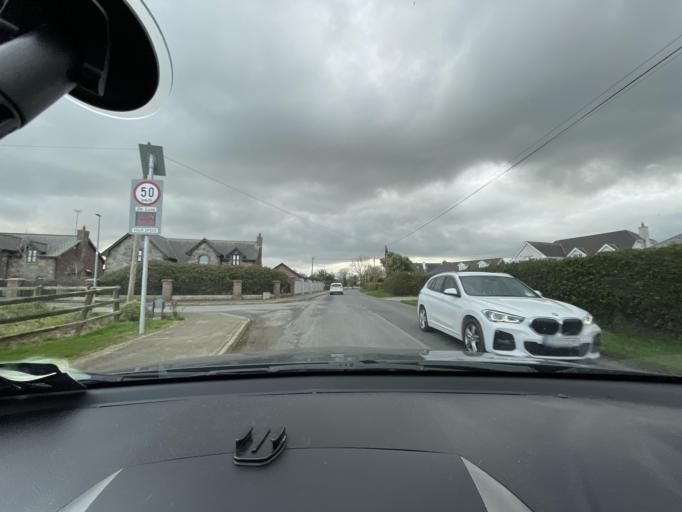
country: IE
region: Leinster
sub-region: Lu
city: Termonfeckin
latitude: 53.7657
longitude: -6.2599
